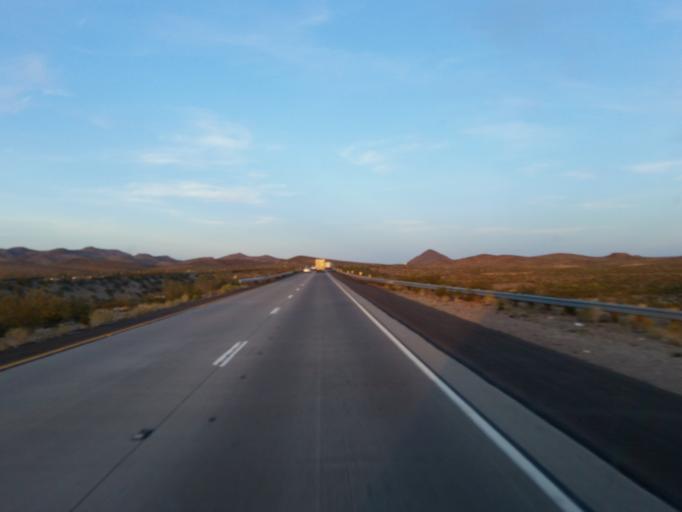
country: US
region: California
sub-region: San Bernardino County
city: Twentynine Palms
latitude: 34.7274
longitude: -115.8301
